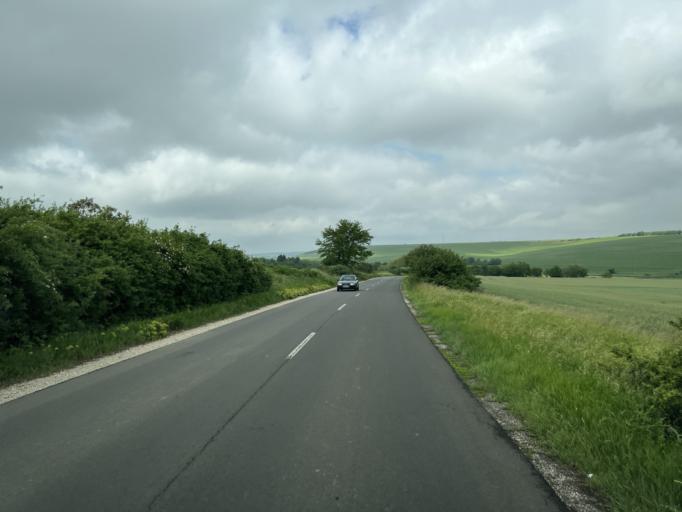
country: HU
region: Pest
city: Kartal
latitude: 47.7298
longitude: 19.5303
